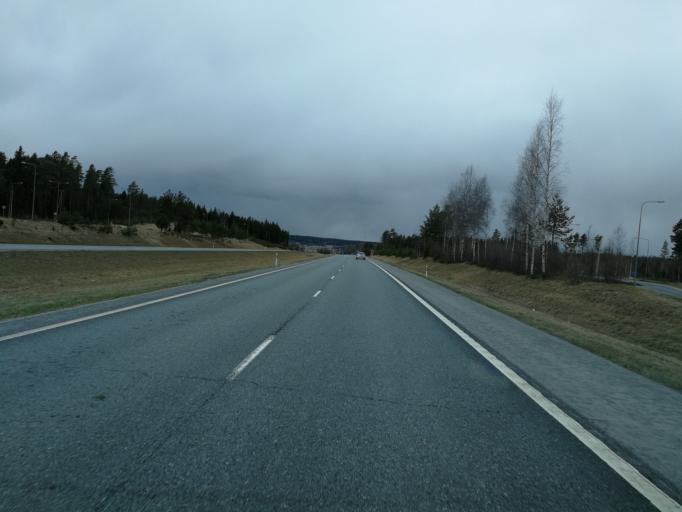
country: FI
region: Varsinais-Suomi
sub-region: Salo
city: Pertteli
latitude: 60.4072
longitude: 23.2140
